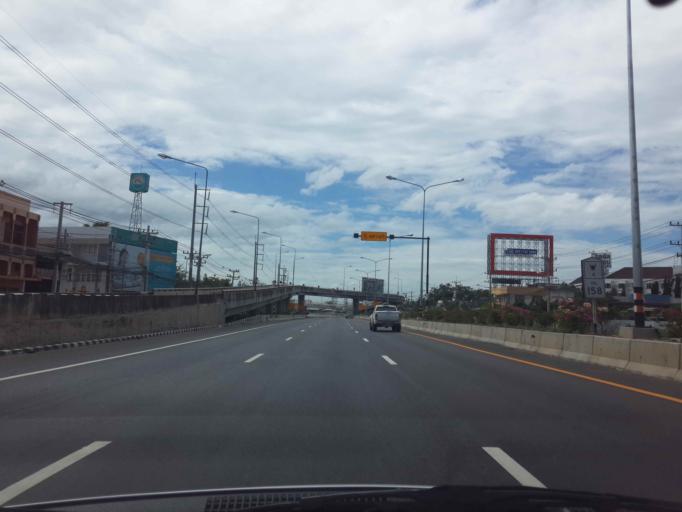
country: TH
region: Phetchaburi
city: Phetchaburi
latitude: 13.1090
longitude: 99.9328
